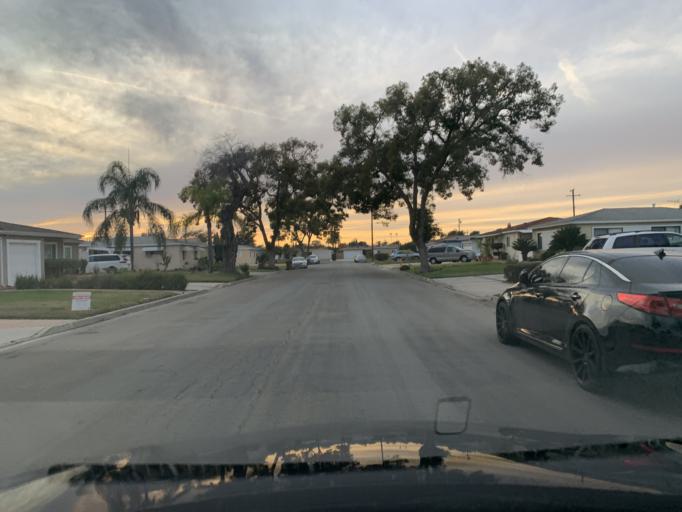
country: US
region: California
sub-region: Orange County
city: Garden Grove
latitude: 33.7832
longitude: -117.9262
